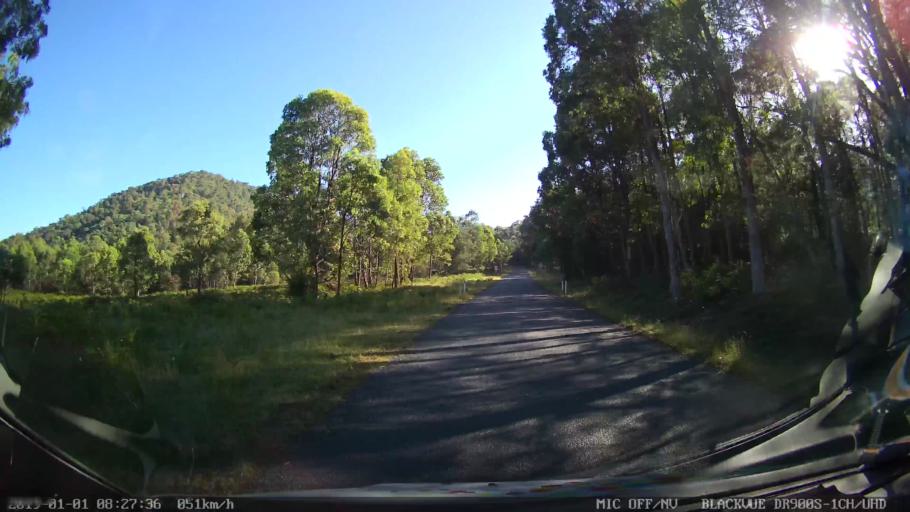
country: AU
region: New South Wales
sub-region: Snowy River
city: Jindabyne
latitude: -36.3804
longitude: 148.1845
